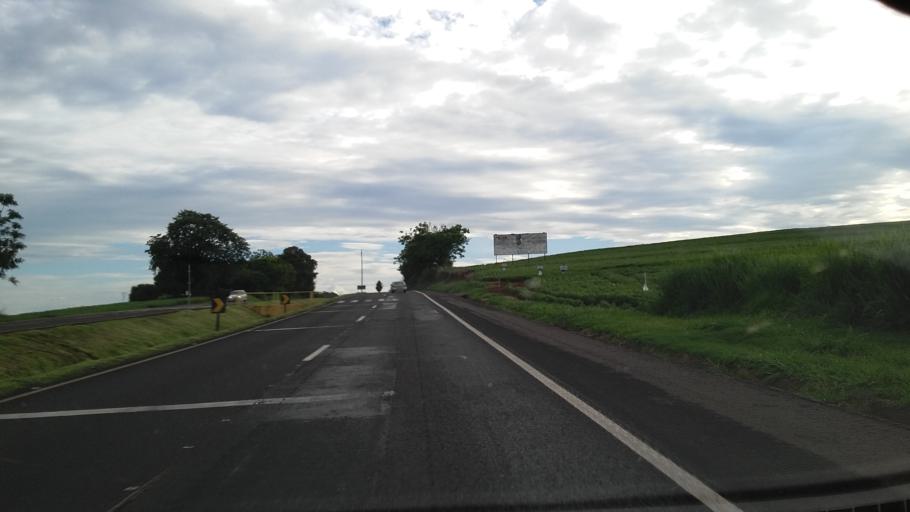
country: BR
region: Parana
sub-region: Paicandu
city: Paicandu
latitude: -23.5142
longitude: -52.0263
